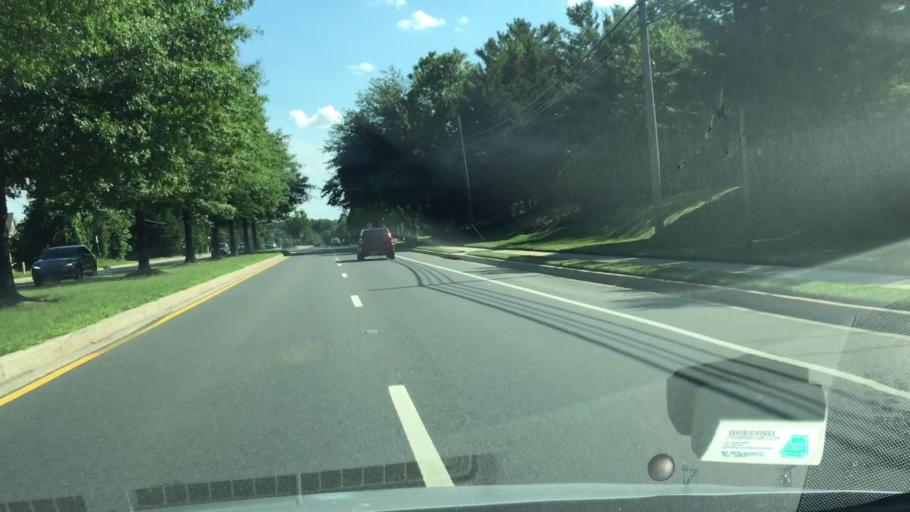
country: US
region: Maryland
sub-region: Montgomery County
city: Layhill
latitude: 39.0869
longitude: -77.0453
